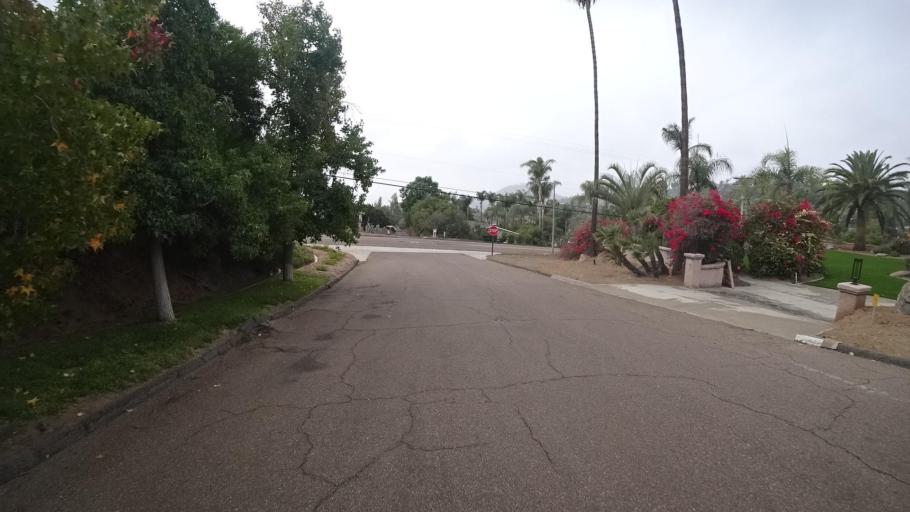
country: US
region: California
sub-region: San Diego County
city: Rancho San Diego
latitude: 32.7717
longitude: -116.9244
